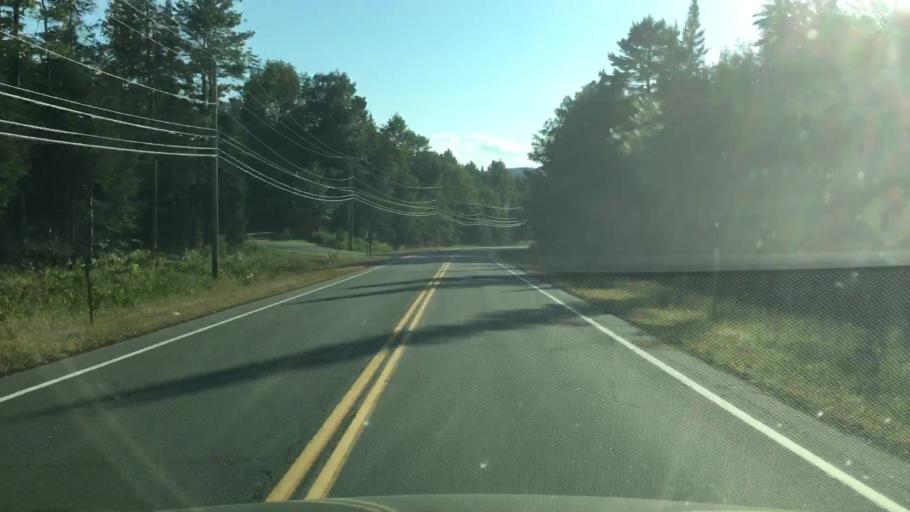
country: US
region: New Hampshire
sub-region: Grafton County
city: Littleton
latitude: 44.3115
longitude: -71.8359
